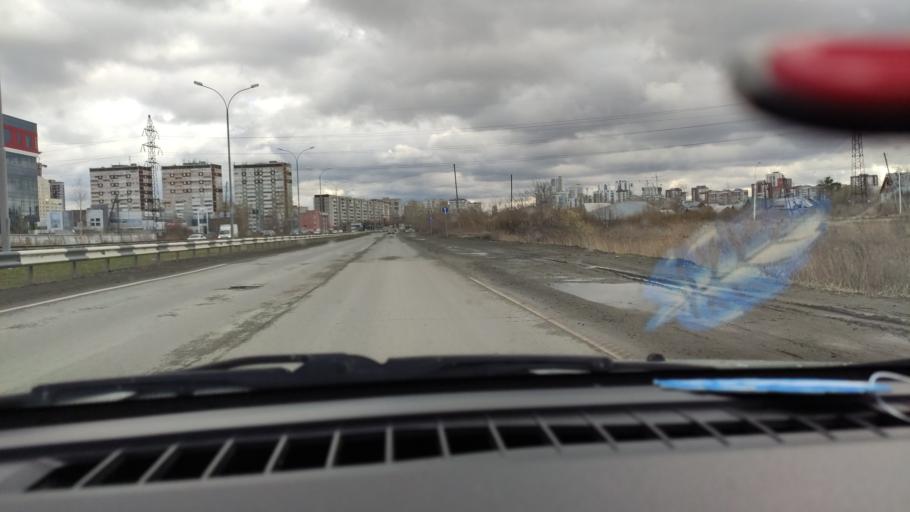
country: RU
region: Sverdlovsk
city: Shirokaya Rechka
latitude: 56.8269
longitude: 60.5286
